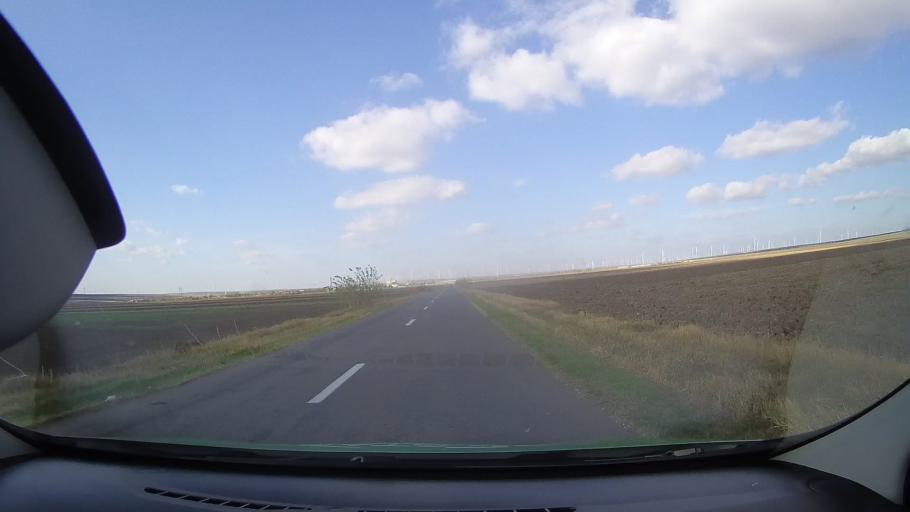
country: RO
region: Constanta
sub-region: Comuna Cogealac
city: Tariverde
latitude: 44.5530
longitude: 28.6232
